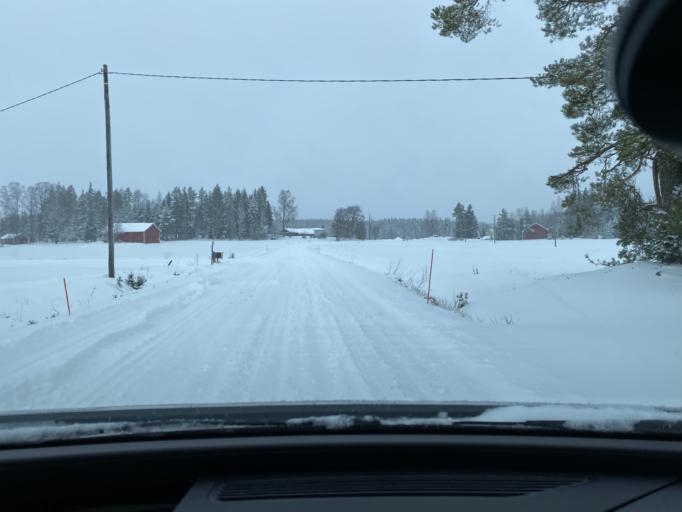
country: FI
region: Haeme
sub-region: Forssa
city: Humppila
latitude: 61.0108
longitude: 23.3030
